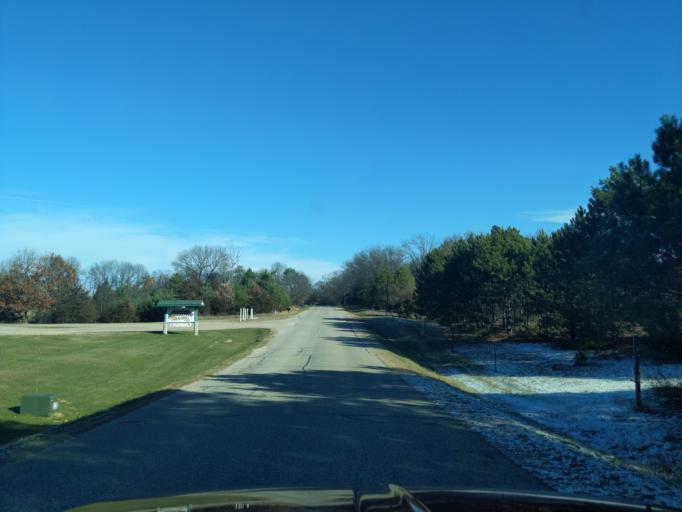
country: US
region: Wisconsin
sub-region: Waushara County
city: Silver Lake
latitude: 44.0888
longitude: -89.1917
